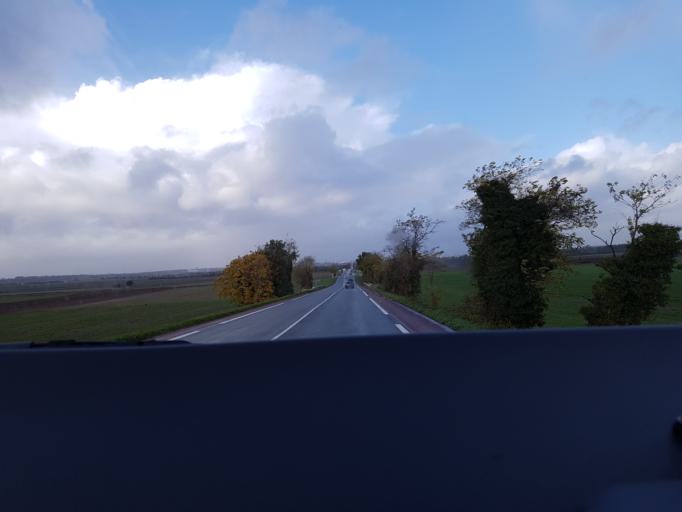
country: FR
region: Poitou-Charentes
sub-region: Departement de la Charente-Maritime
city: Les Gonds
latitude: 45.6809
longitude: -0.6081
